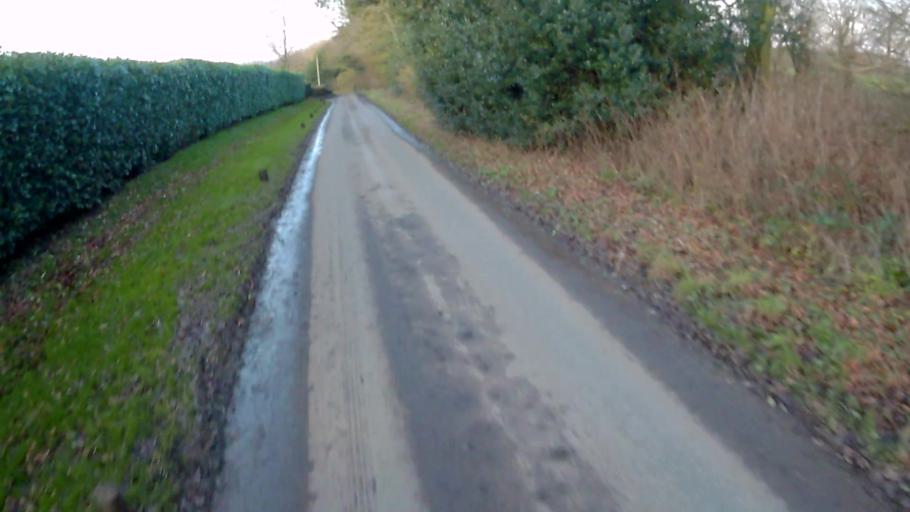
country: GB
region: England
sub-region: Hampshire
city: Overton
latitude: 51.2218
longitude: -1.2237
